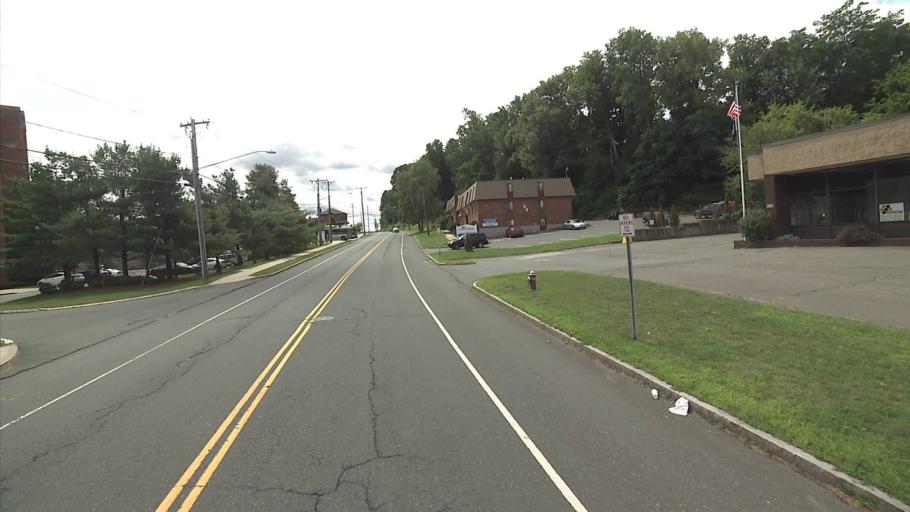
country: US
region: Connecticut
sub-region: Hartford County
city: New Britain
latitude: 41.6888
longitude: -72.7600
